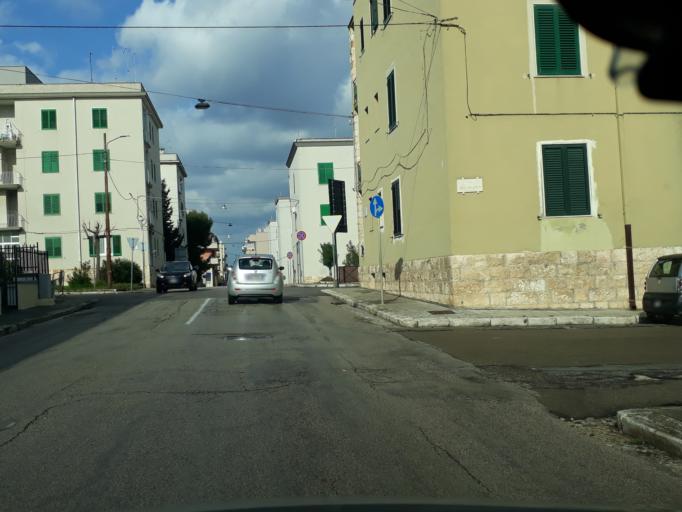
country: IT
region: Apulia
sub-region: Provincia di Brindisi
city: Fasano
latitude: 40.8303
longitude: 17.3556
